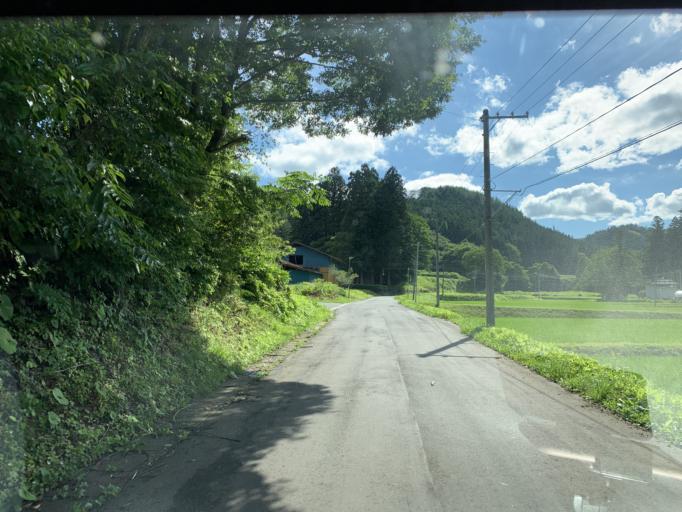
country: JP
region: Iwate
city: Ichinoseki
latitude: 38.9165
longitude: 140.9835
